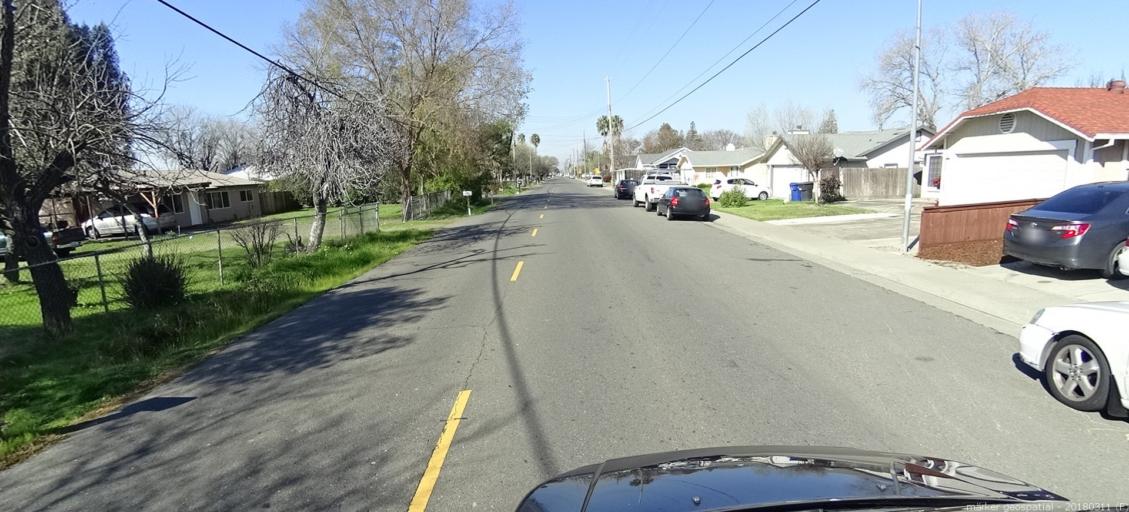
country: US
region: California
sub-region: Sacramento County
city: Florin
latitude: 38.4653
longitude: -121.3967
